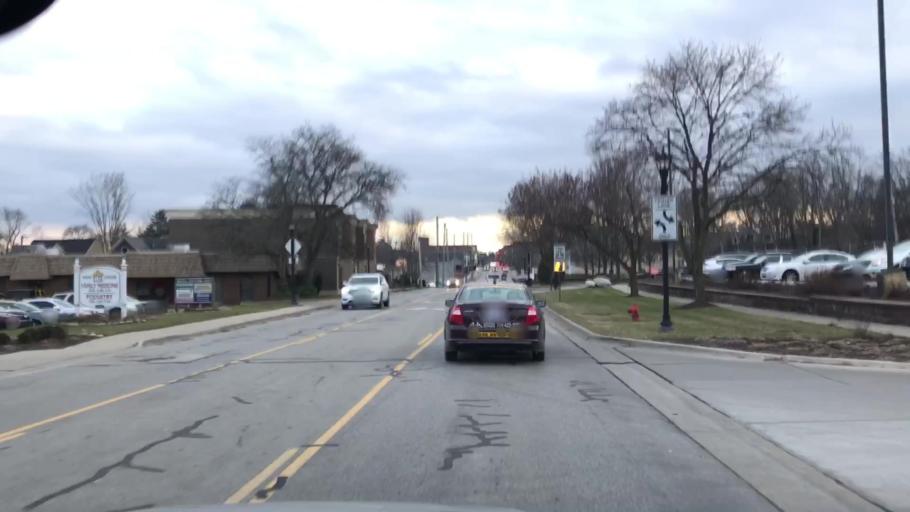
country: US
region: Michigan
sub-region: Wayne County
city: Northville
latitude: 42.4355
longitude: -83.4832
